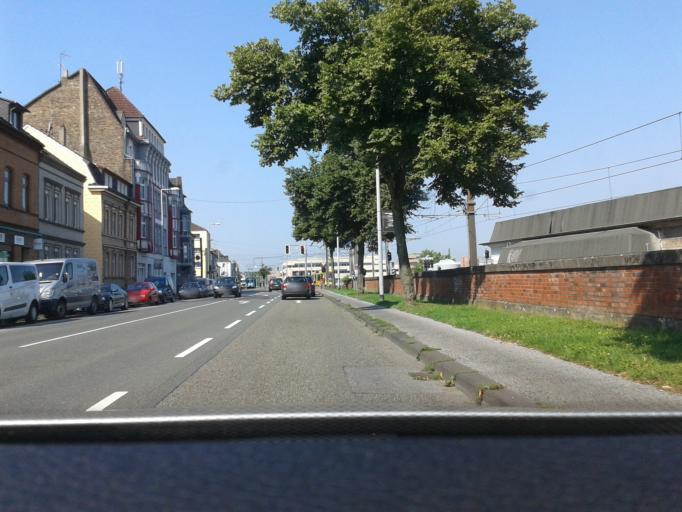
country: DE
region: North Rhine-Westphalia
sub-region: Regierungsbezirk Dusseldorf
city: Muelheim (Ruhr)
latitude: 51.4263
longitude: 6.8649
